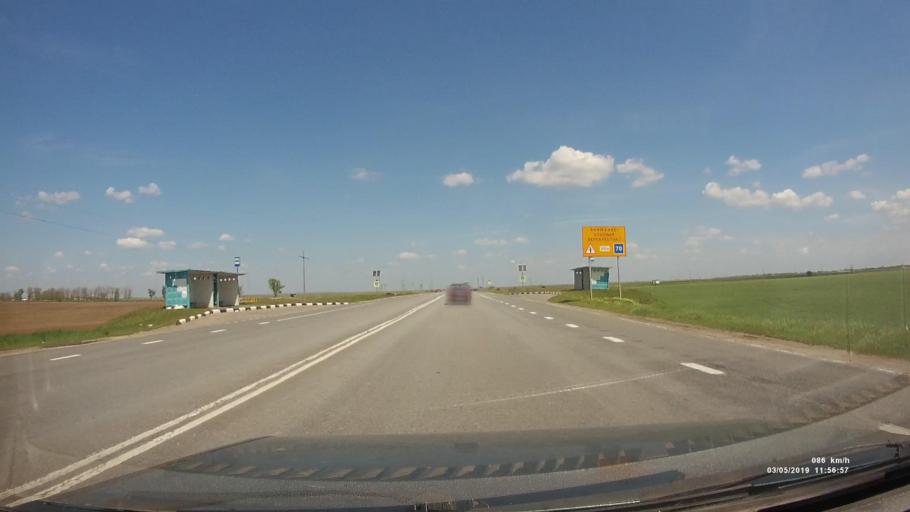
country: RU
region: Rostov
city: Bagayevskaya
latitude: 47.2004
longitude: 40.3062
